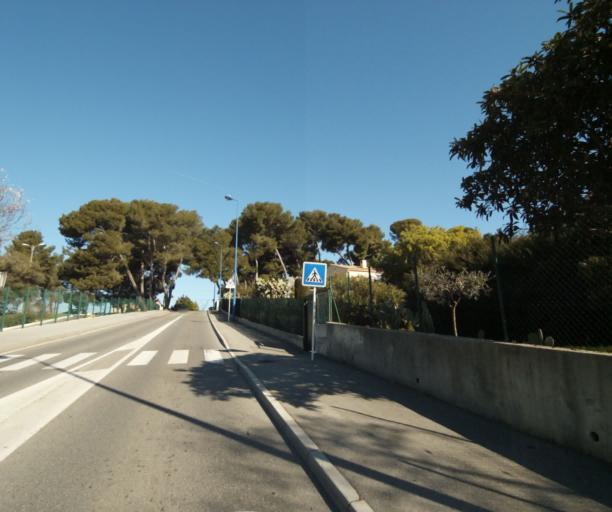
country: FR
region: Provence-Alpes-Cote d'Azur
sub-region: Departement des Alpes-Maritimes
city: Biot
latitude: 43.6036
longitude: 7.0920
